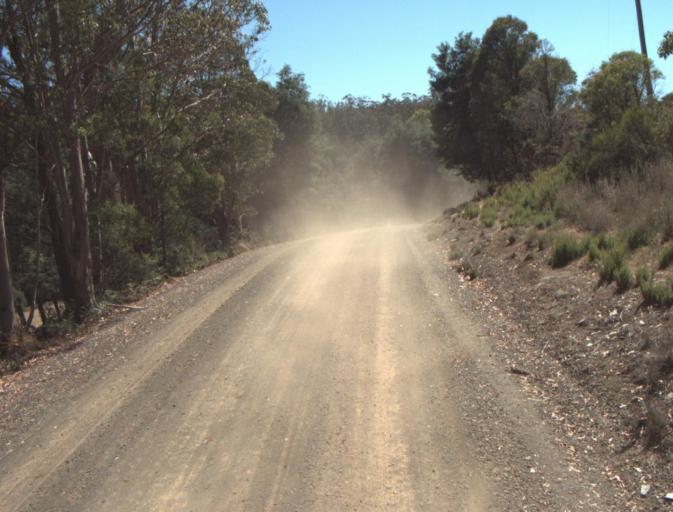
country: AU
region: Tasmania
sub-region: Launceston
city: Newstead
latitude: -41.2998
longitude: 147.3349
